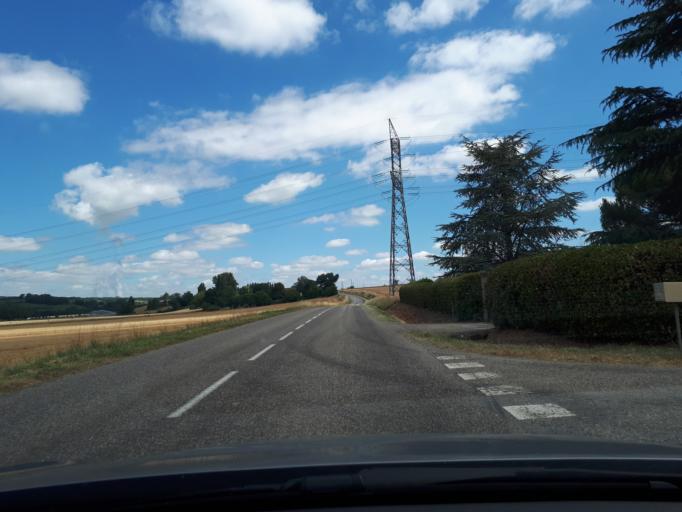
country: FR
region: Midi-Pyrenees
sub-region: Departement du Tarn-et-Garonne
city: Auvillar
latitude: 44.0391
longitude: 0.8549
